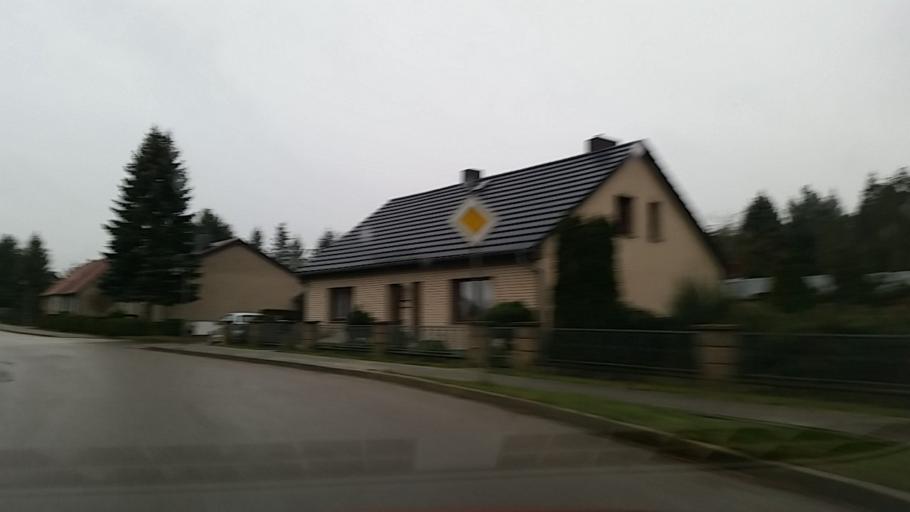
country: DE
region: Brandenburg
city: Gumtow
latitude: 53.0246
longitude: 12.2435
